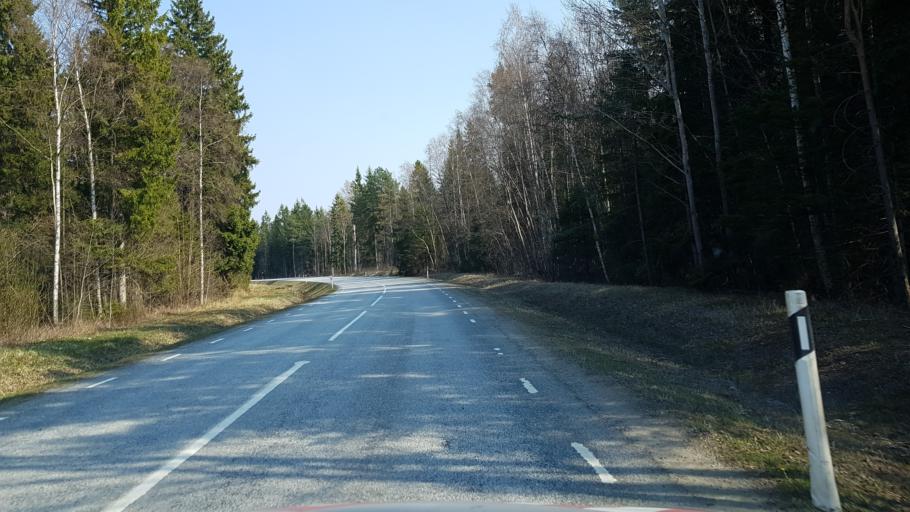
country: EE
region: Harju
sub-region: Paldiski linn
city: Paldiski
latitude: 59.2497
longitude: 23.8885
